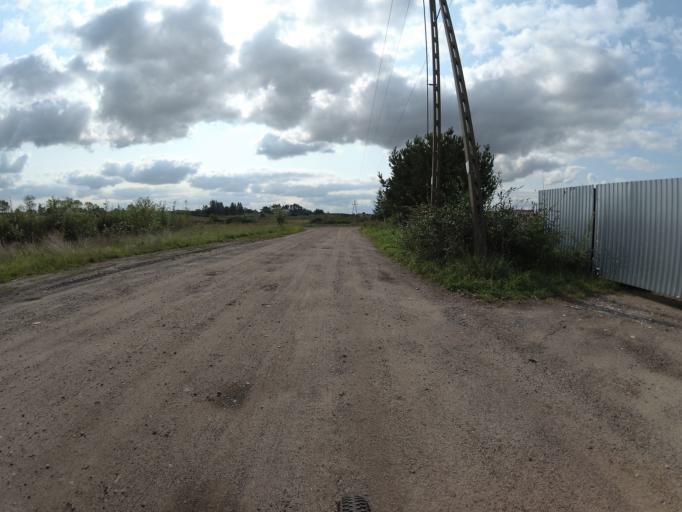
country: PL
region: Pomeranian Voivodeship
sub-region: Powiat wejherowski
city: Bojano
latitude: 54.4993
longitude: 18.4279
